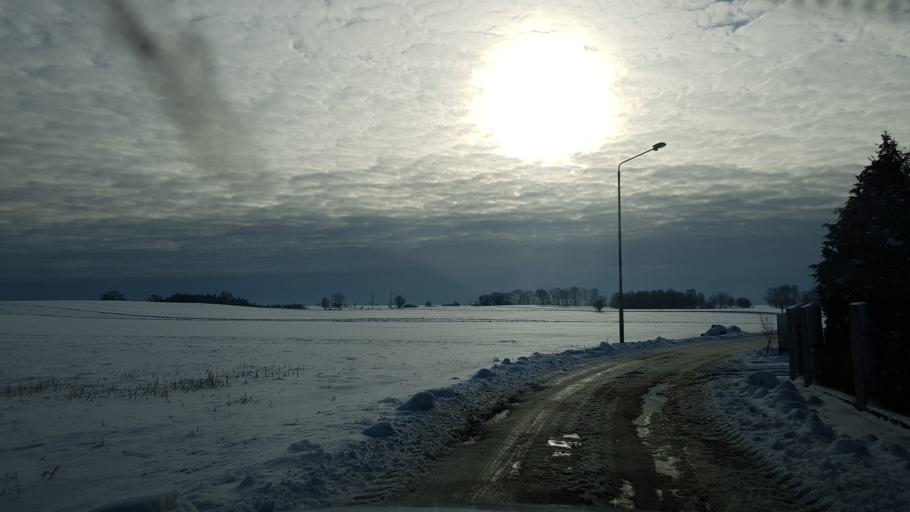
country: PL
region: West Pomeranian Voivodeship
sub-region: Powiat drawski
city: Drawsko Pomorskie
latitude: 53.5384
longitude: 15.7842
